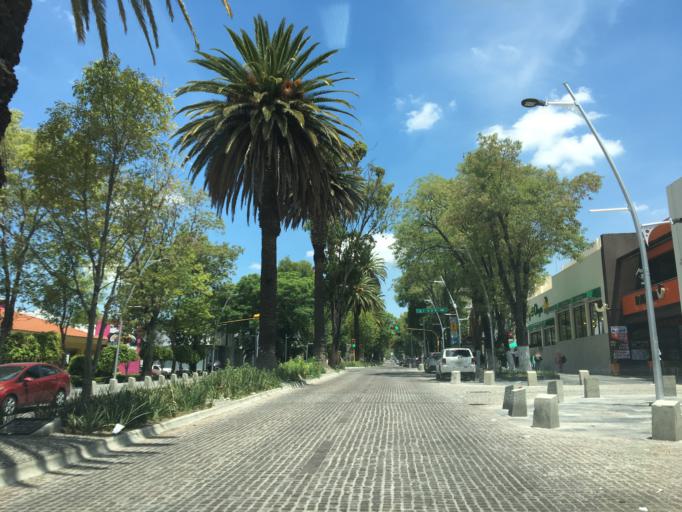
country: MX
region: Puebla
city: Puebla
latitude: 19.0496
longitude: -98.2142
